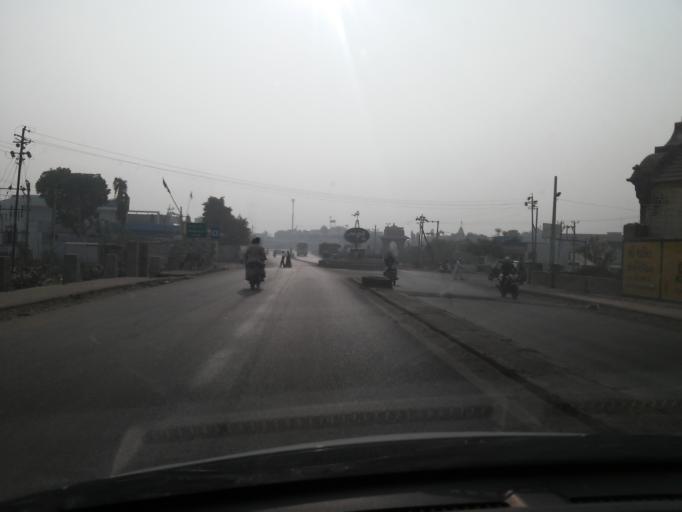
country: IN
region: Gujarat
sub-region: Kachchh
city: Bhuj
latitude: 23.2408
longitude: 69.7104
